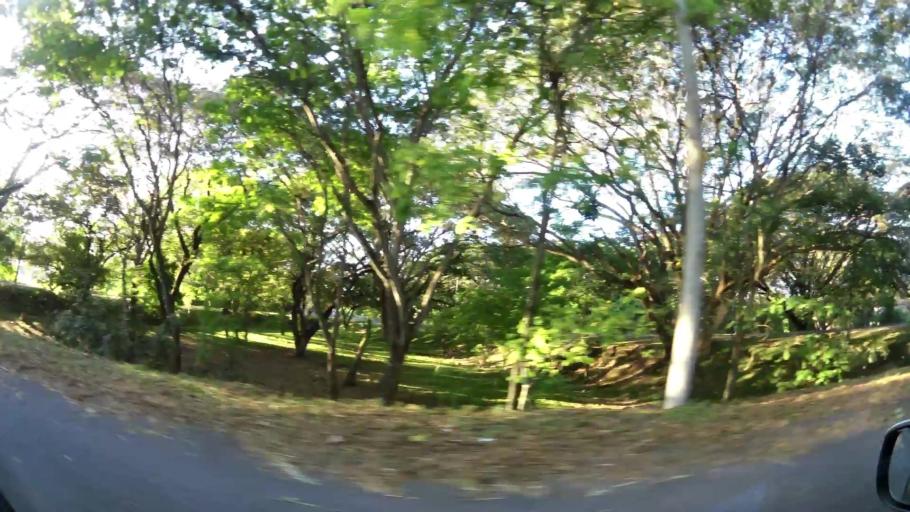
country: CR
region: Puntarenas
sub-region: Canton Central de Puntarenas
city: Chacarita
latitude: 9.9758
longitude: -84.7394
